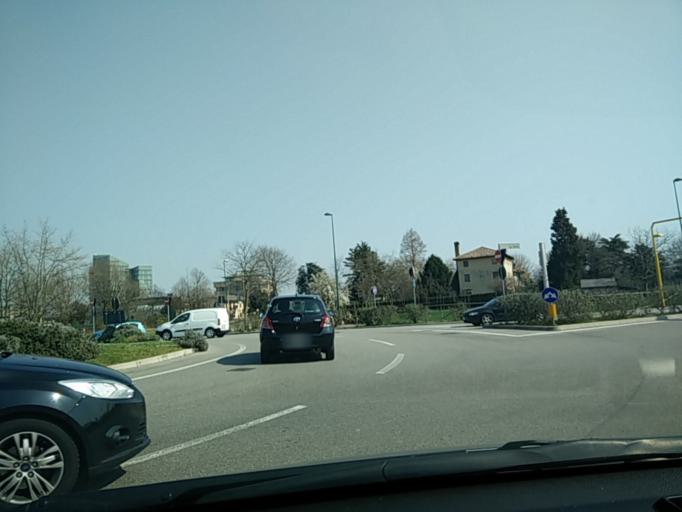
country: IT
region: Veneto
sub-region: Provincia di Venezia
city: Zelarino
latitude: 45.5094
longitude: 12.2288
